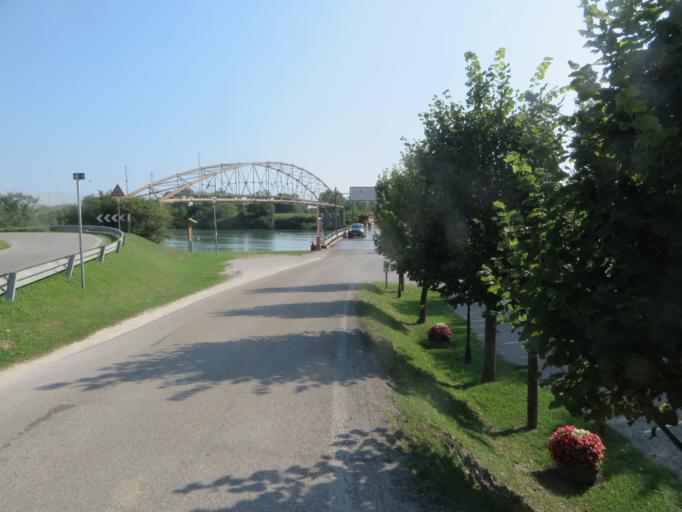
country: IT
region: Veneto
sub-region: Provincia di Venezia
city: Crepaldo
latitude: 45.5454
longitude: 12.7258
